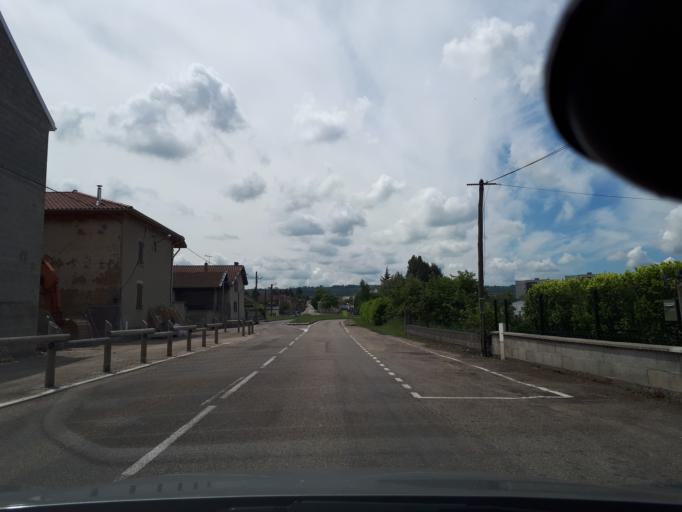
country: FR
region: Rhone-Alpes
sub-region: Departement de l'Isere
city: Bourgoin-Jallieu
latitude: 45.6133
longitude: 5.2748
